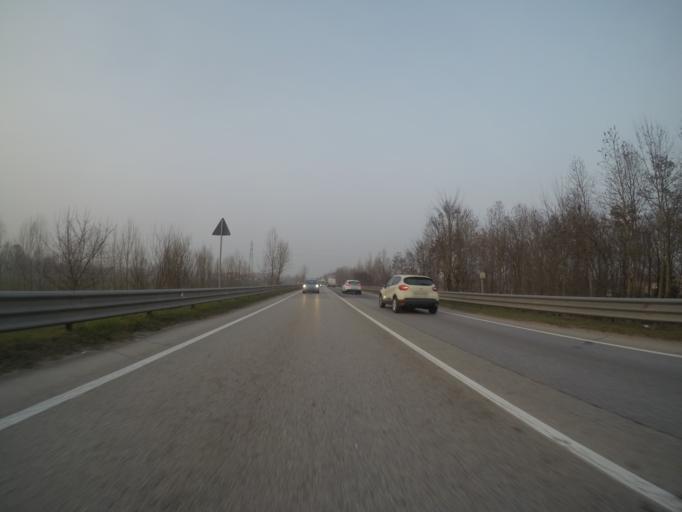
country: IT
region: Veneto
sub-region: Provincia di Padova
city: Camposampiero
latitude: 45.5742
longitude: 11.9556
